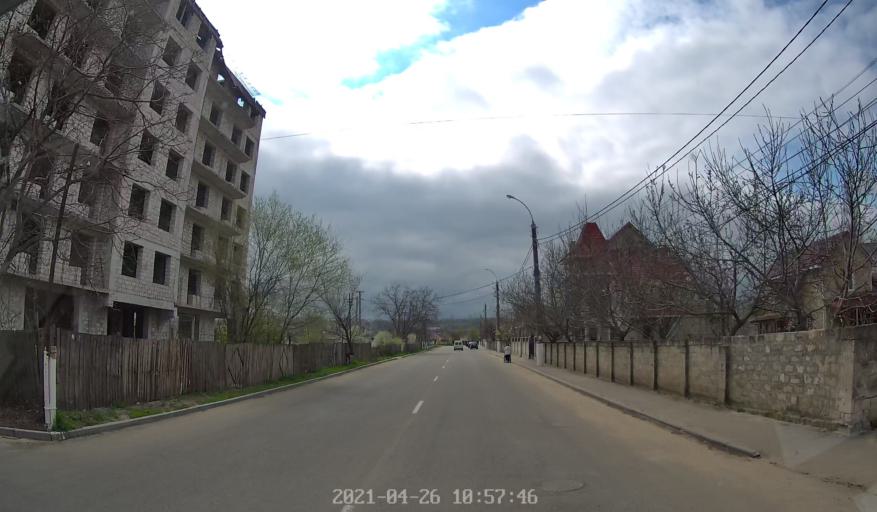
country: MD
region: Chisinau
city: Cricova
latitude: 47.1384
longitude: 28.8663
